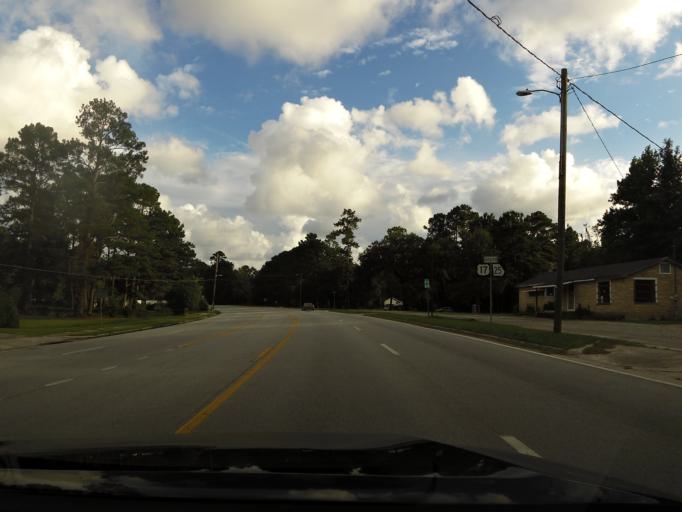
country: US
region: Georgia
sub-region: Liberty County
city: Midway
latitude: 31.7430
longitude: -81.4400
